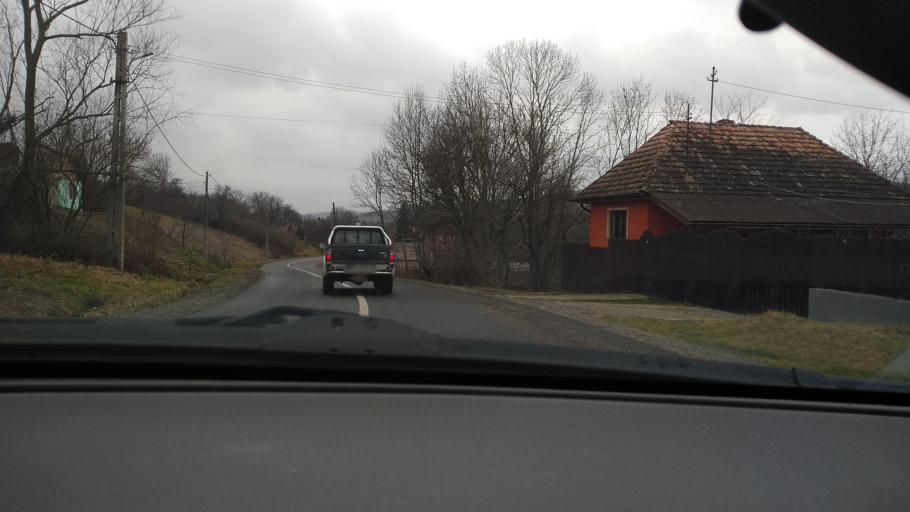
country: RO
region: Mures
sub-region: Comuna Bereni
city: Bereni
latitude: 46.5581
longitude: 24.8725
